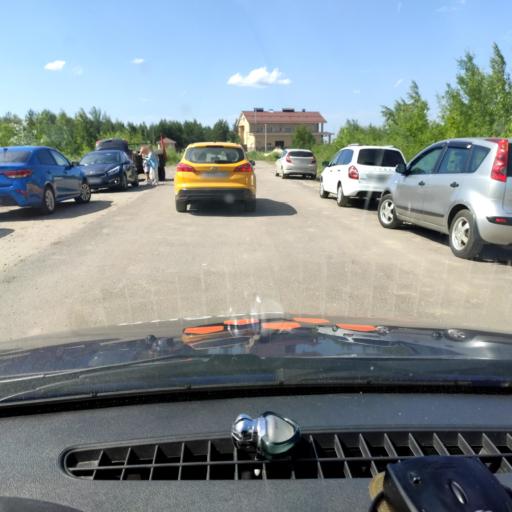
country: RU
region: Voronezj
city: Somovo
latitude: 51.7787
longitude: 39.2948
